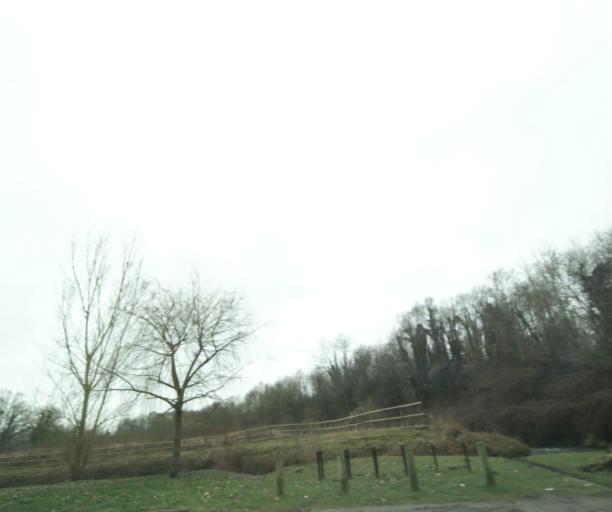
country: FR
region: Ile-de-France
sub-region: Departement de l'Essonne
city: Champlan
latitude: 48.7042
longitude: 2.2684
